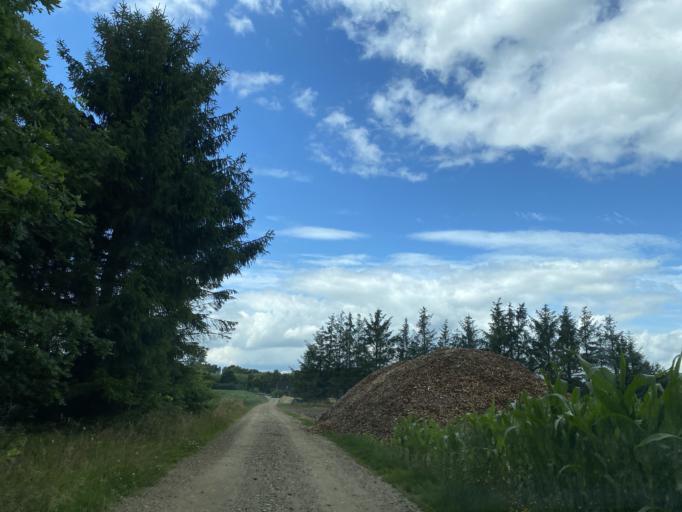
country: DK
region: Central Jutland
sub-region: Viborg Kommune
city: Bjerringbro
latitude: 56.2871
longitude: 9.6548
